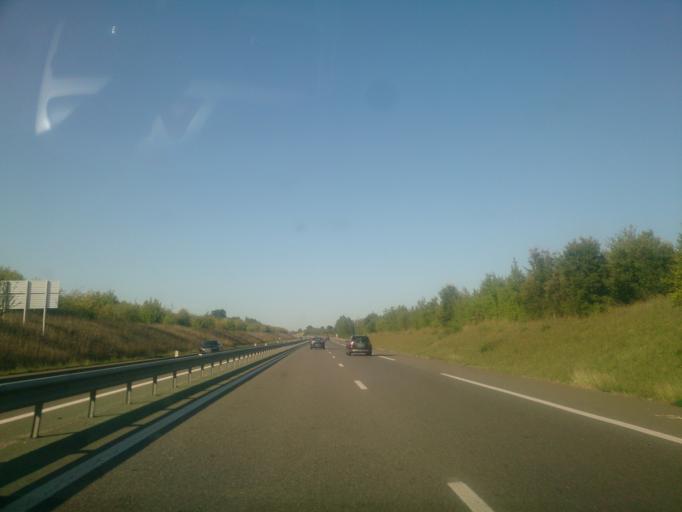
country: FR
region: Midi-Pyrenees
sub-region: Departement du Tarn-et-Garonne
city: Caussade
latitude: 44.1638
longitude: 1.5215
